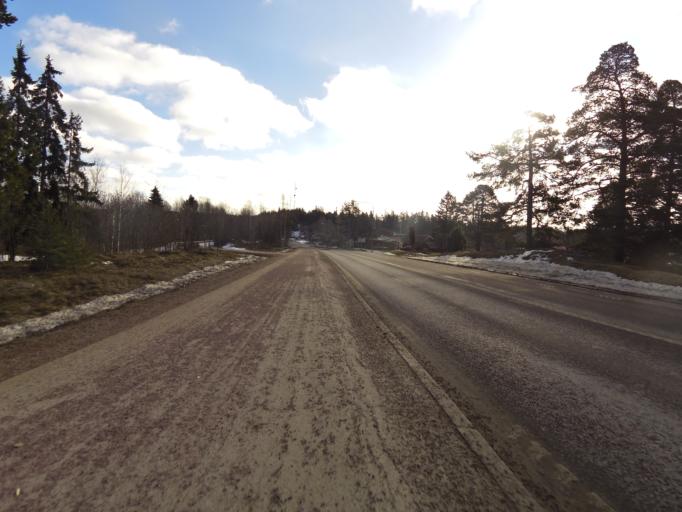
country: SE
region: Gaevleborg
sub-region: Gavle Kommun
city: Gavle
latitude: 60.6508
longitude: 17.1826
